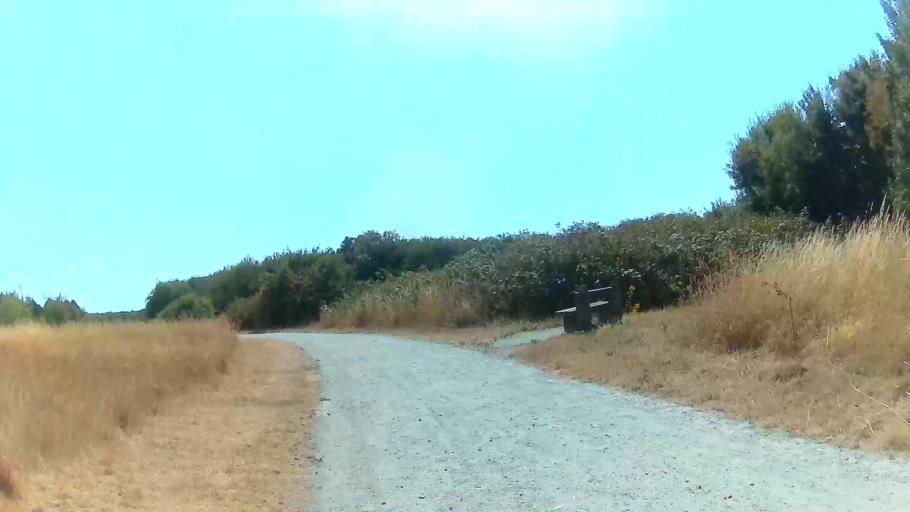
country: GB
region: England
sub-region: Greater London
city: Elm Park
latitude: 51.5296
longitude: 0.1922
